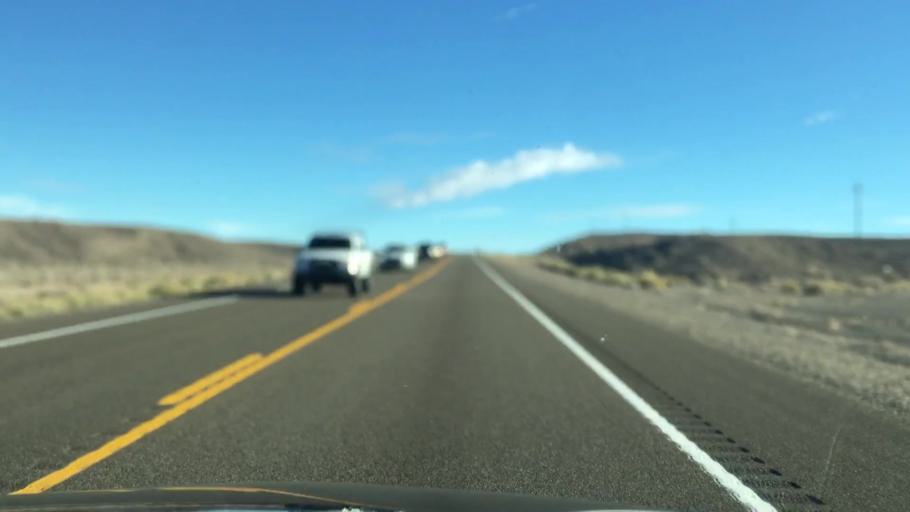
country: US
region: Nevada
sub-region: Mineral County
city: Hawthorne
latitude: 38.2211
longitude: -118.0095
